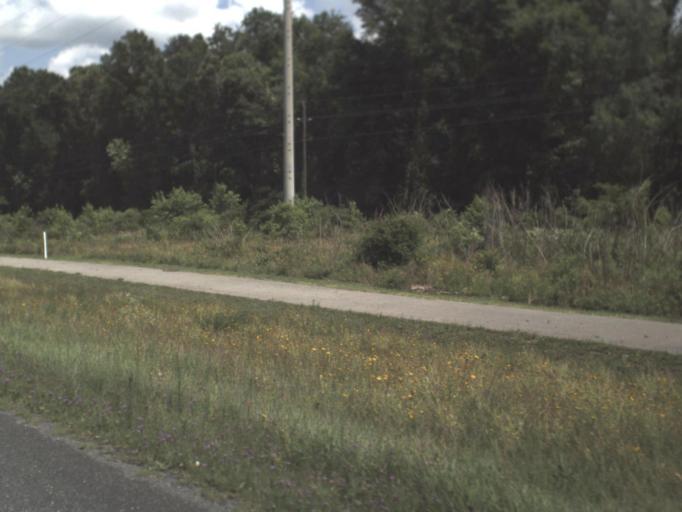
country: US
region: Florida
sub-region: Alachua County
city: High Springs
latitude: 29.9524
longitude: -82.8305
